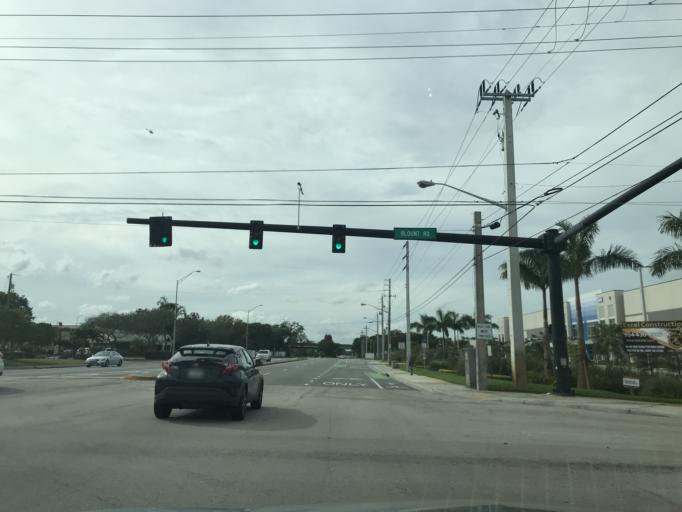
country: US
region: Florida
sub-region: Broward County
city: Coconut Creek
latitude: 26.2601
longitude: -80.1639
